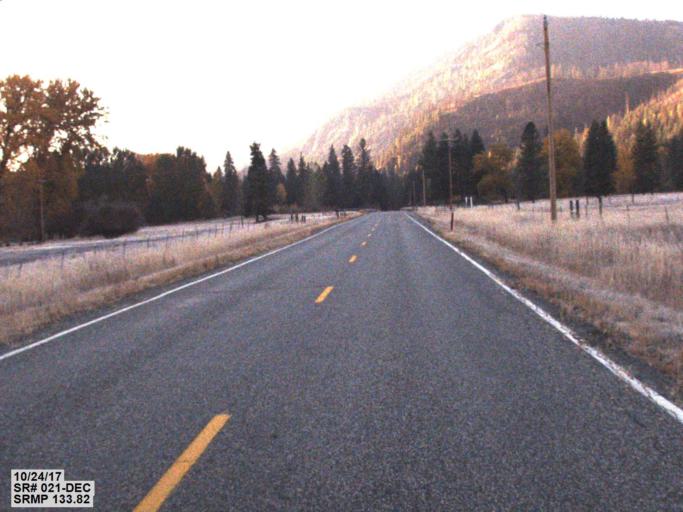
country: US
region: Washington
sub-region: Ferry County
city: Republic
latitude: 48.3040
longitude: -118.7363
